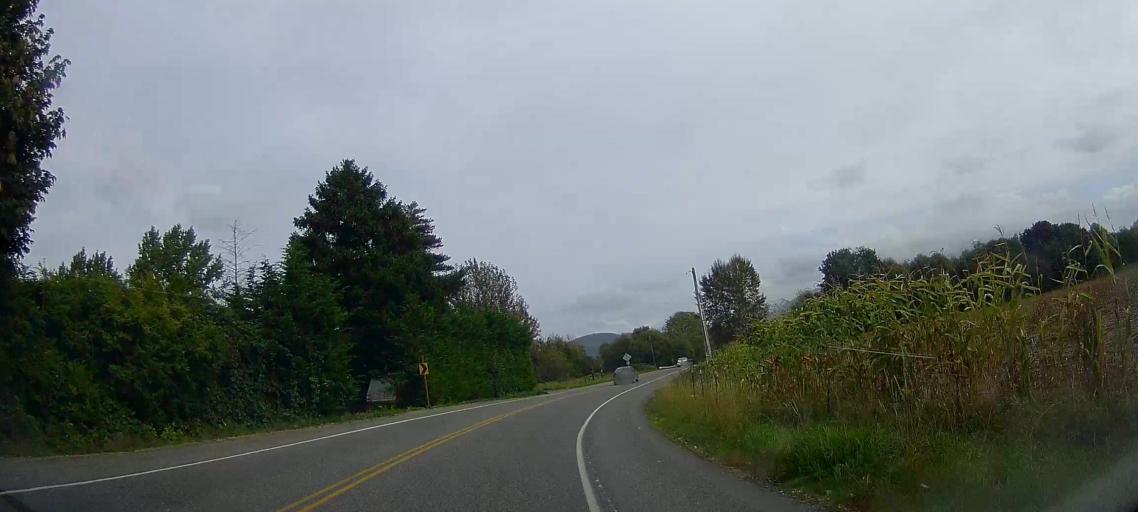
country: US
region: Washington
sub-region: Skagit County
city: Burlington
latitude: 48.4672
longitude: -122.2970
